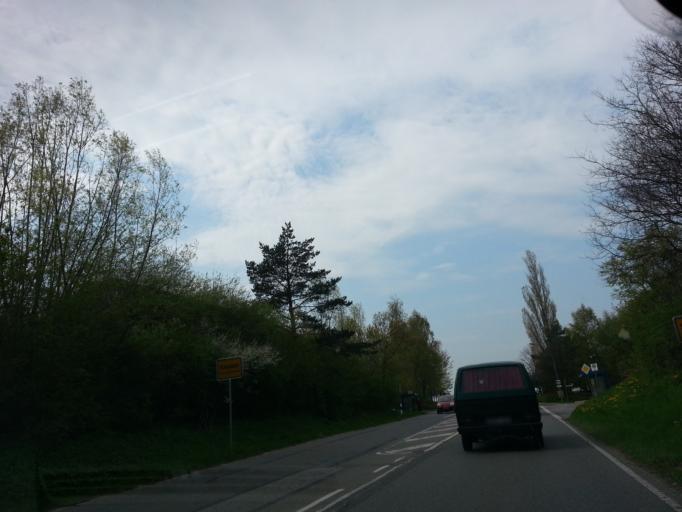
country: DE
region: Schleswig-Holstein
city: Scharbeutz
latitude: 54.0219
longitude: 10.7523
